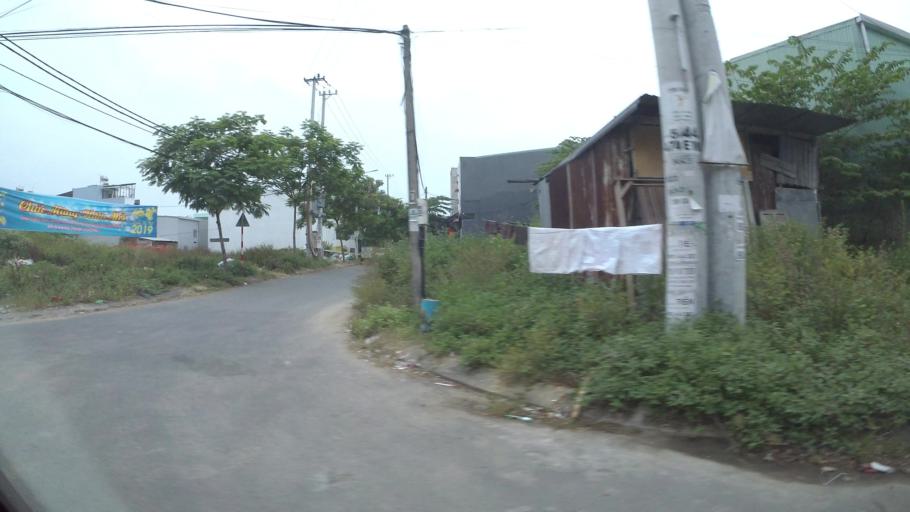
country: VN
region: Da Nang
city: Thanh Khe
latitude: 16.0463
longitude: 108.1767
